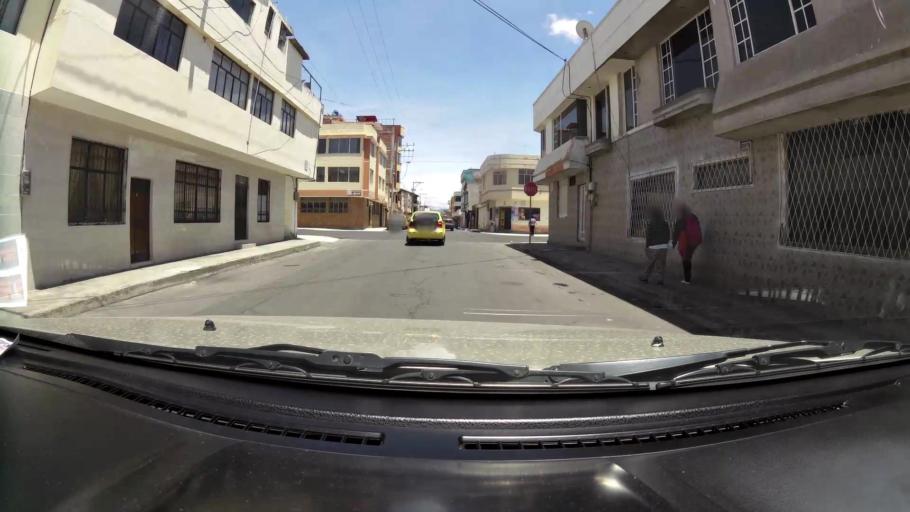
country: EC
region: Chimborazo
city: Riobamba
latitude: -1.6793
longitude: -78.6485
